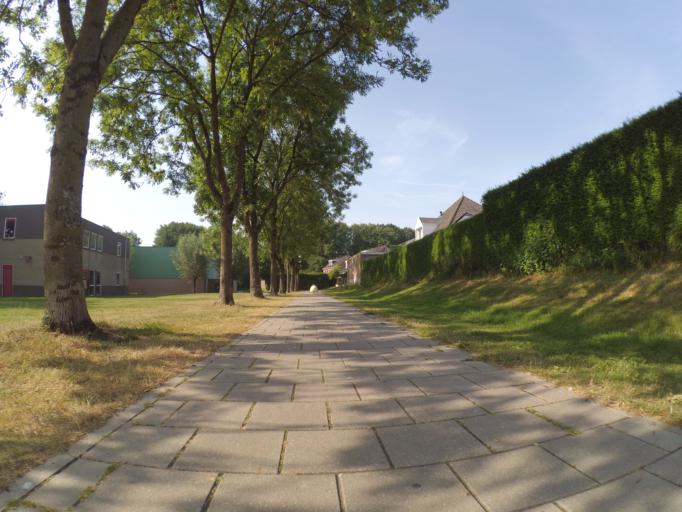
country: DE
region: Lower Saxony
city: Getelo
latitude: 52.4070
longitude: 6.9024
